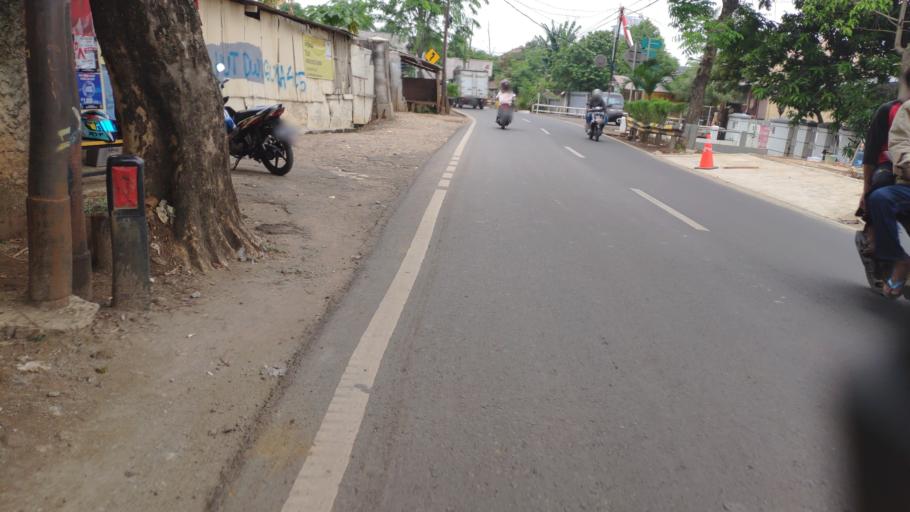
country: ID
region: West Java
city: Depok
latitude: -6.3459
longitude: 106.8224
